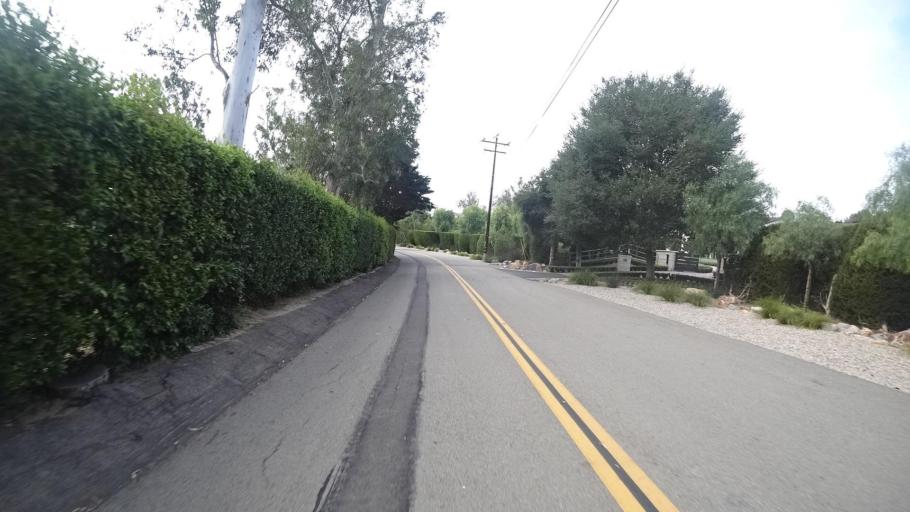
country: US
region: California
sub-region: San Diego County
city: Rancho Santa Fe
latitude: 33.0088
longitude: -117.2085
